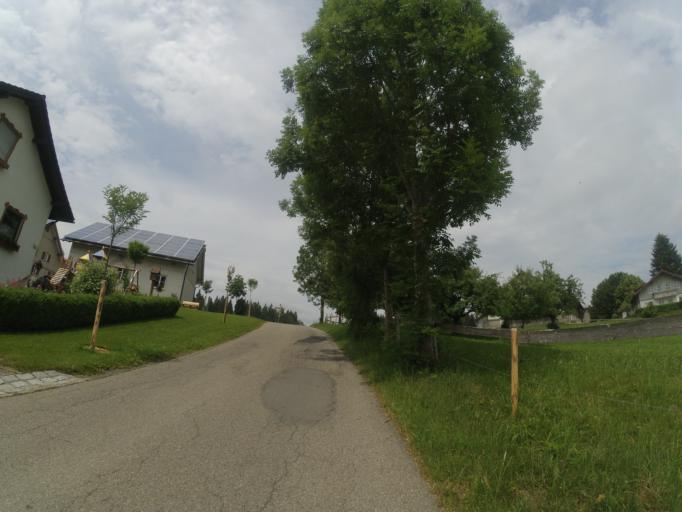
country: DE
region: Baden-Wuerttemberg
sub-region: Tuebingen Region
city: Leutkirch im Allgau
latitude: 47.7578
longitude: 9.9985
